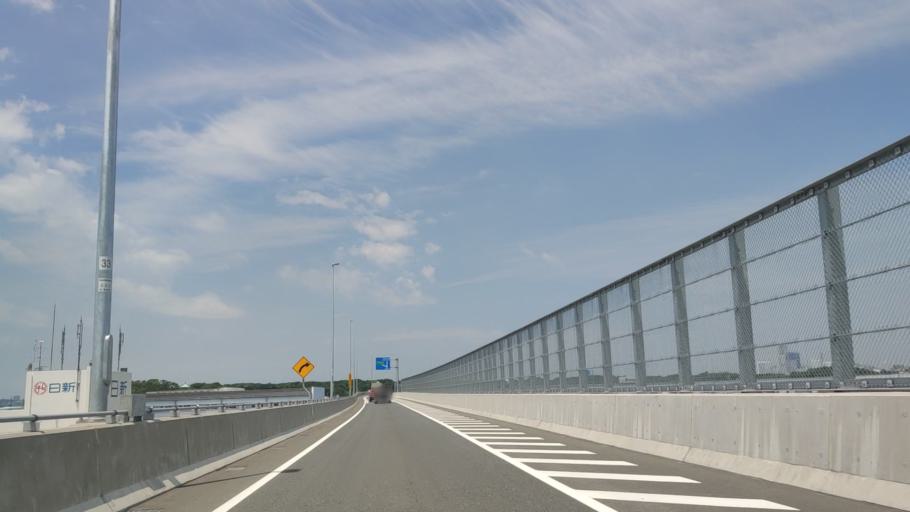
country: JP
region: Kanagawa
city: Yokohama
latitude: 35.4144
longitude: 139.6738
